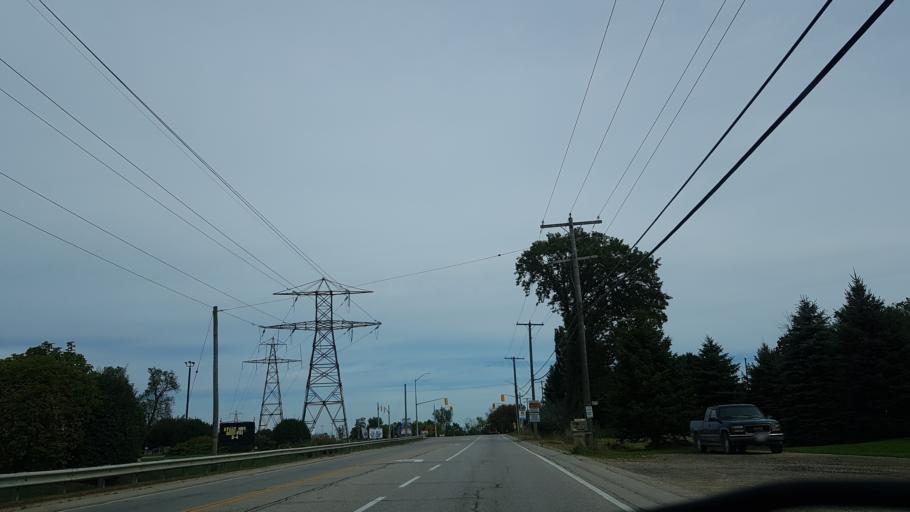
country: CA
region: Ontario
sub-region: Wellington County
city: Guelph
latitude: 43.5036
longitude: -80.2690
